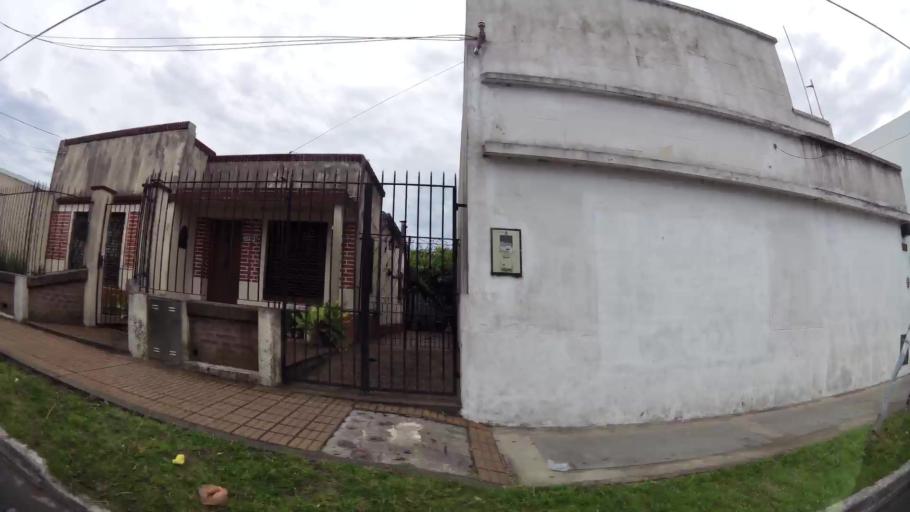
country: AR
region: Buenos Aires
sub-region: Partido de Quilmes
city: Quilmes
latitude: -34.7515
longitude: -58.2141
